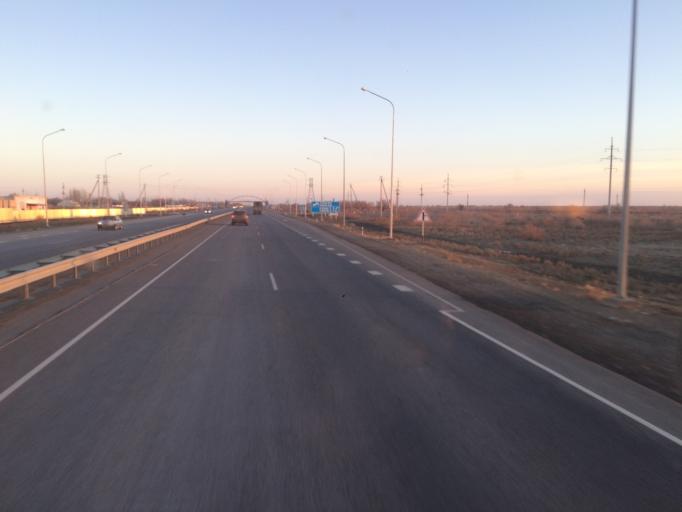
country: KZ
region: Qyzylorda
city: Shieli
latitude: 44.1416
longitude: 66.9616
